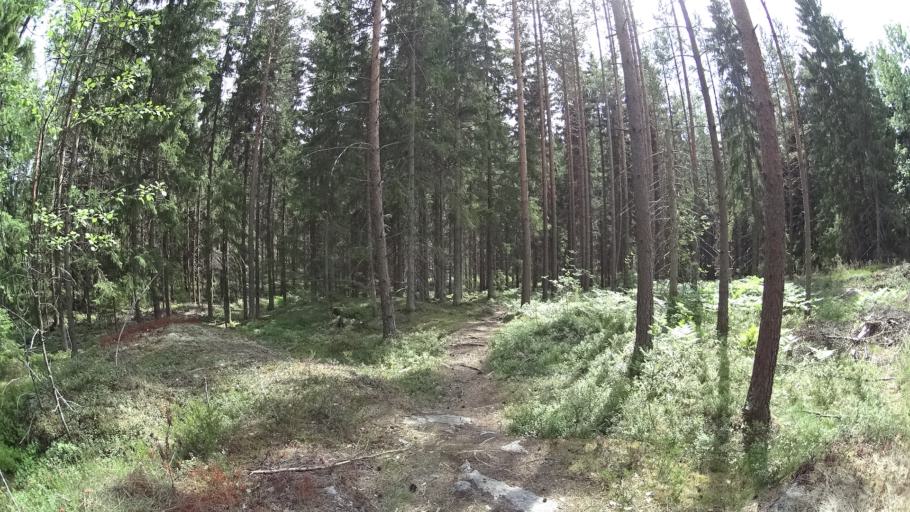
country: FI
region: Uusimaa
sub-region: Helsinki
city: Espoo
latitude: 60.1898
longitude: 24.6619
